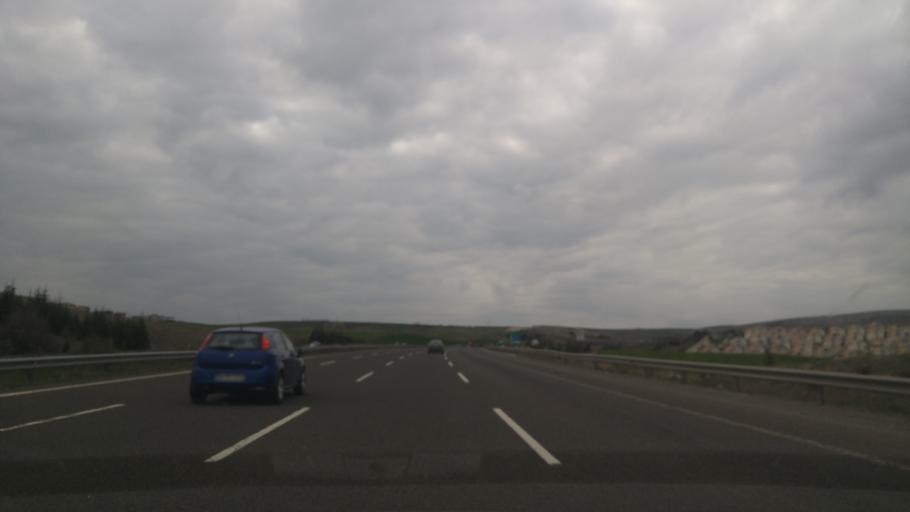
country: TR
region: Ankara
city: Etimesgut
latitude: 39.8467
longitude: 32.6326
